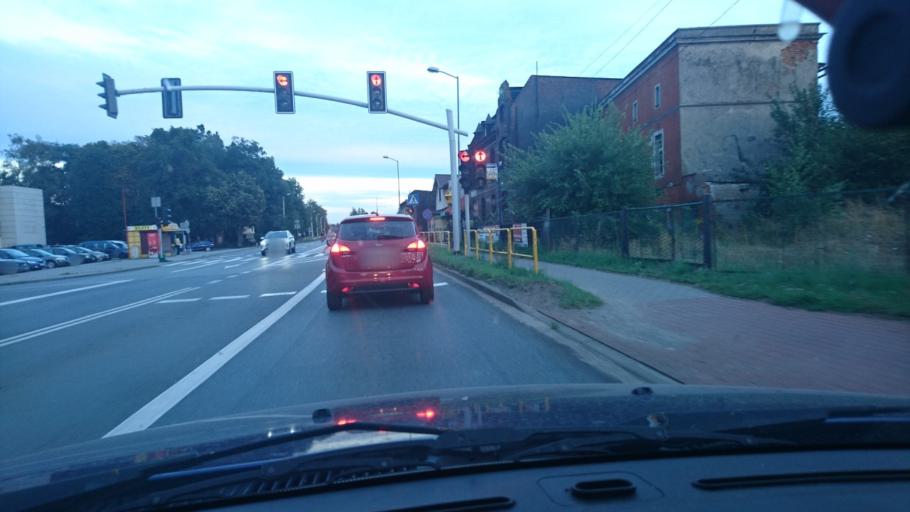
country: PL
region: Silesian Voivodeship
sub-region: Powiat tarnogorski
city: Tarnowskie Gory
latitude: 50.4746
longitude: 18.7987
